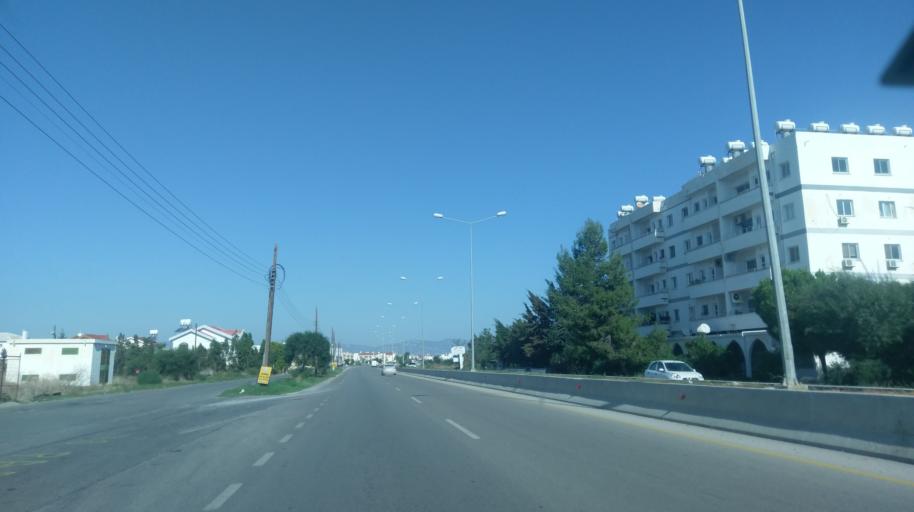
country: CY
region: Ammochostos
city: Famagusta
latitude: 35.1909
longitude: 33.8938
